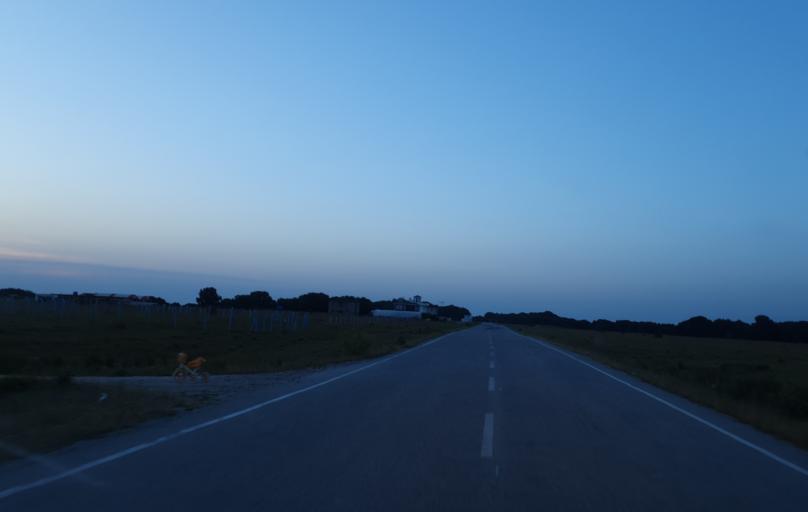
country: TR
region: Tekirdag
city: Cerkezkoey
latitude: 41.3426
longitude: 27.9280
